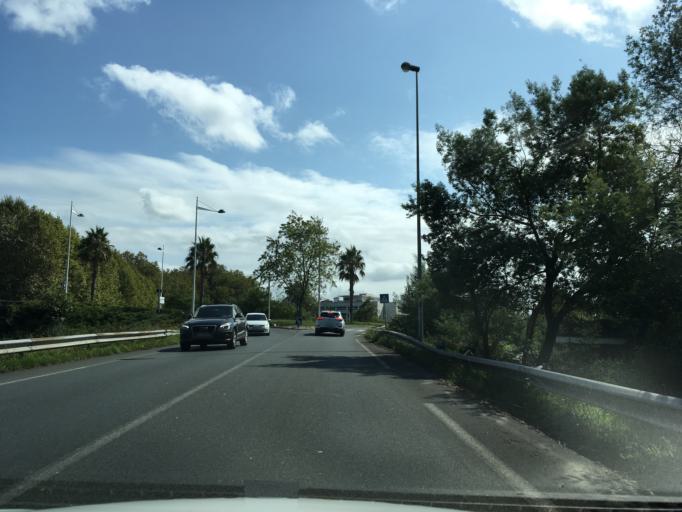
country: FR
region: Aquitaine
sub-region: Departement des Pyrenees-Atlantiques
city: Bayonne
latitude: 43.4868
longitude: -1.4901
